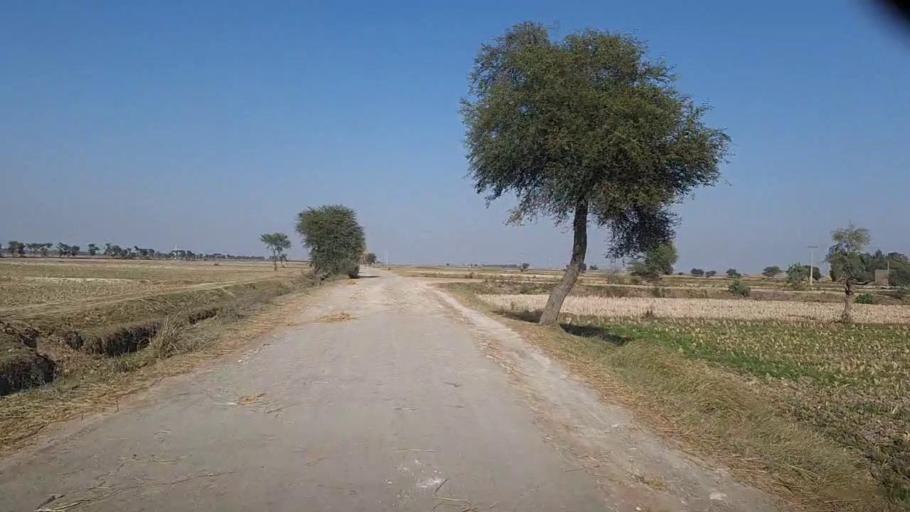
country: PK
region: Sindh
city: Thul
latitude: 28.3562
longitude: 68.7653
